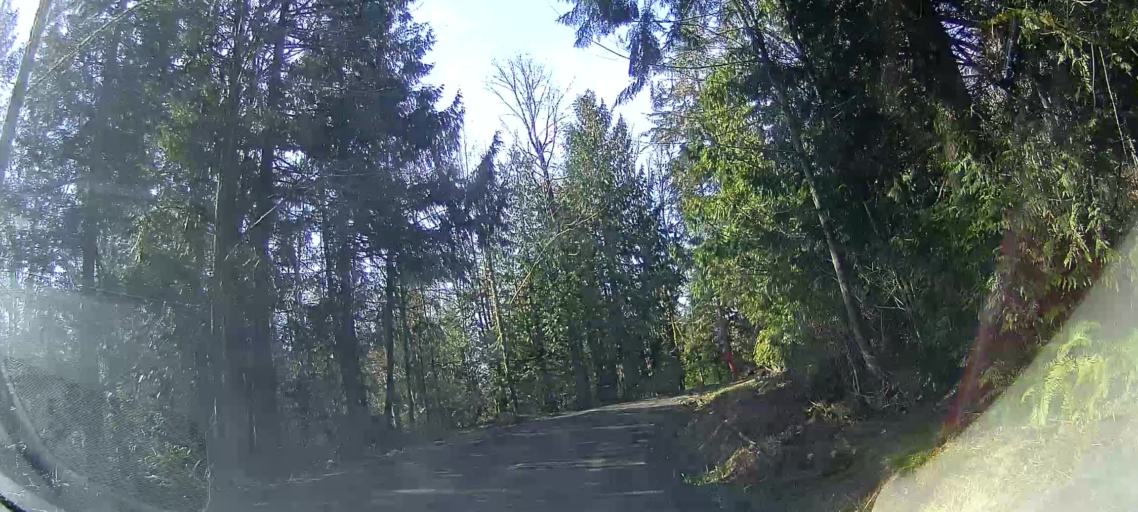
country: US
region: Washington
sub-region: Skagit County
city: Burlington
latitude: 48.5875
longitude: -122.3870
